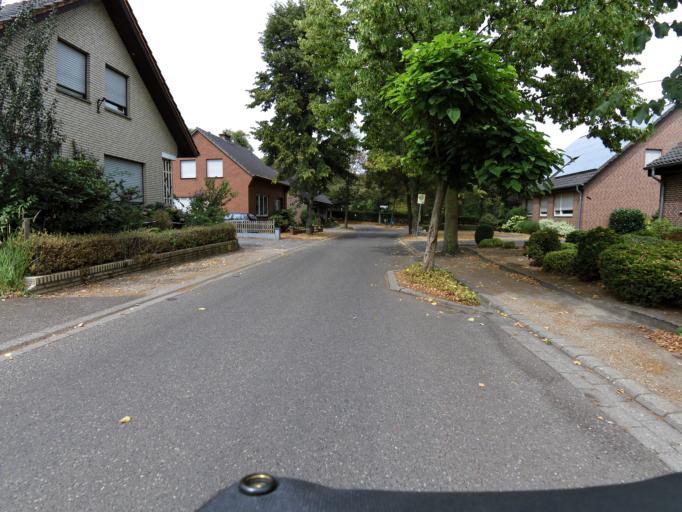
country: DE
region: North Rhine-Westphalia
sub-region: Regierungsbezirk Dusseldorf
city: Kevelaer
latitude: 51.5553
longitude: 6.2122
